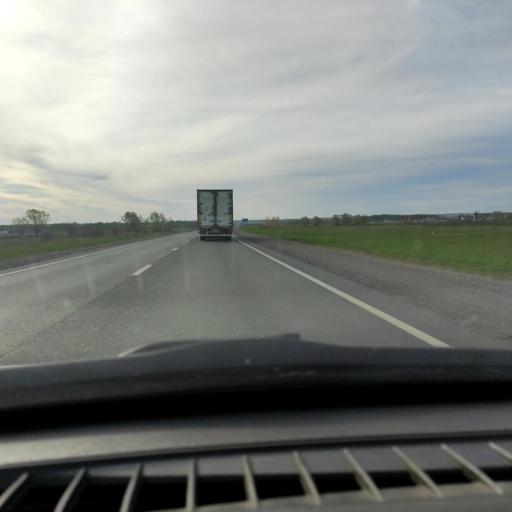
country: RU
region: Samara
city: Krasnyy Yar
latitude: 53.5116
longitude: 50.4164
